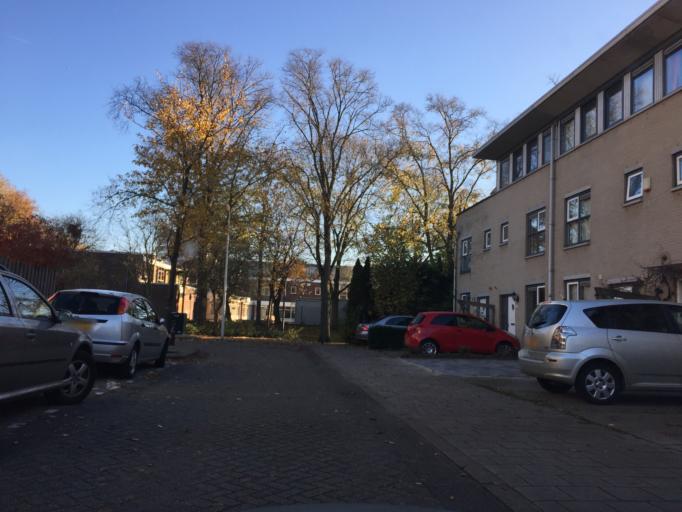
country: NL
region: South Holland
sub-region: Gemeente Westland
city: Kwintsheul
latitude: 52.0352
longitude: 4.2631
